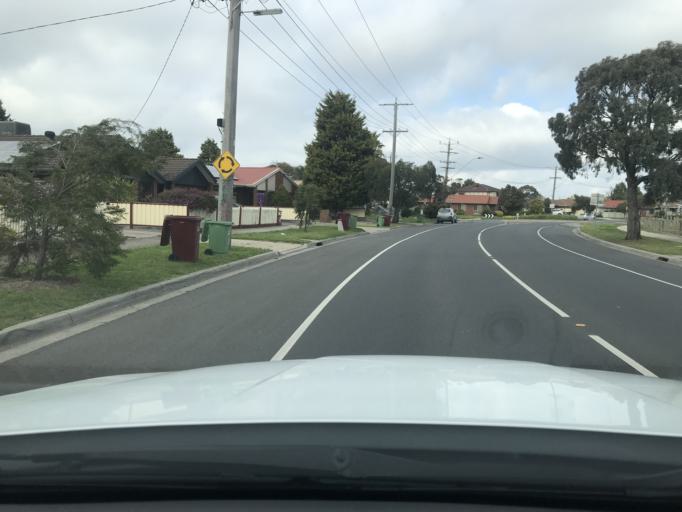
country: AU
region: Victoria
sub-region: Hume
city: Craigieburn
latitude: -37.6103
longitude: 144.9360
